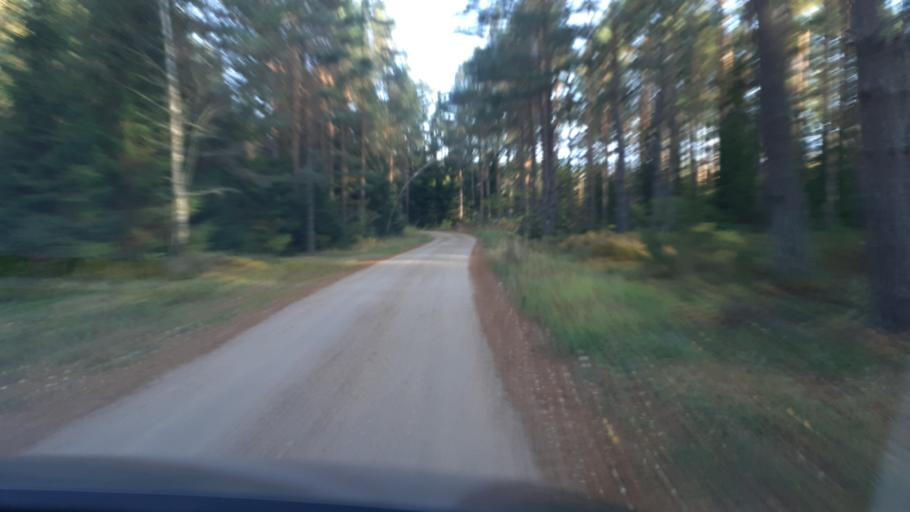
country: LV
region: Kuldigas Rajons
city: Kuldiga
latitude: 56.8591
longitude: 22.1051
